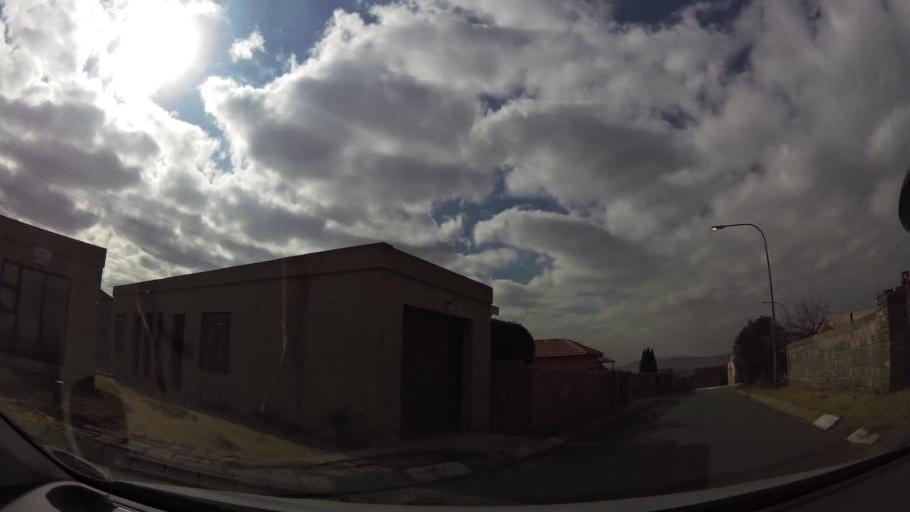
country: ZA
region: Gauteng
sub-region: City of Johannesburg Metropolitan Municipality
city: Roodepoort
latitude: -26.2117
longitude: 27.9071
